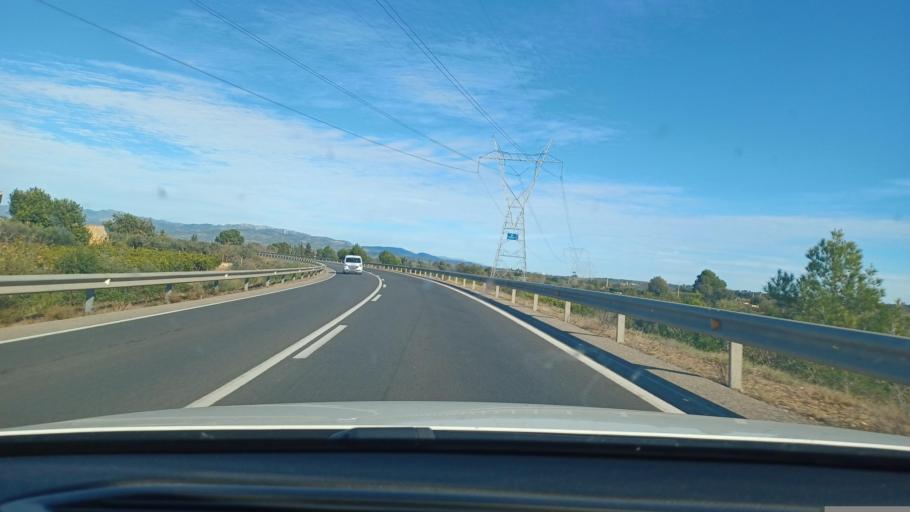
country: ES
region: Catalonia
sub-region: Provincia de Tarragona
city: Santa Barbara
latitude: 40.7087
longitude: 0.5058
